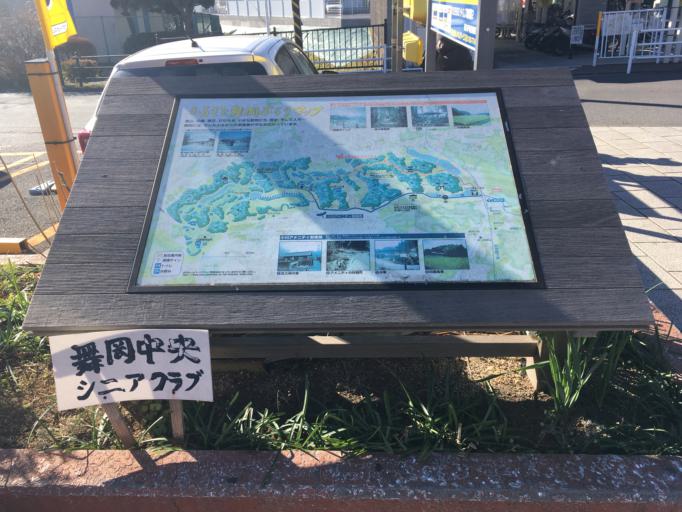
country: JP
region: Kanagawa
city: Kamakura
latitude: 35.4024
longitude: 139.5510
